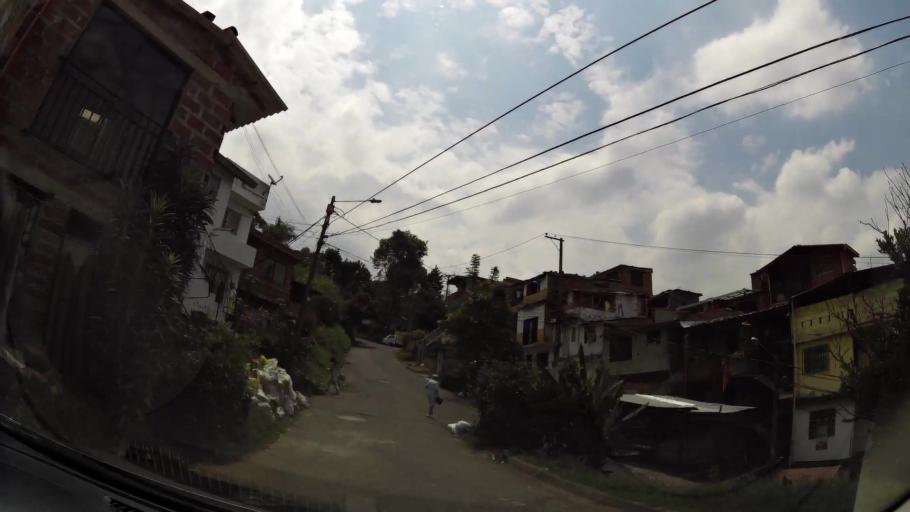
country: CO
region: Antioquia
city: Medellin
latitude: 6.2625
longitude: -75.5471
